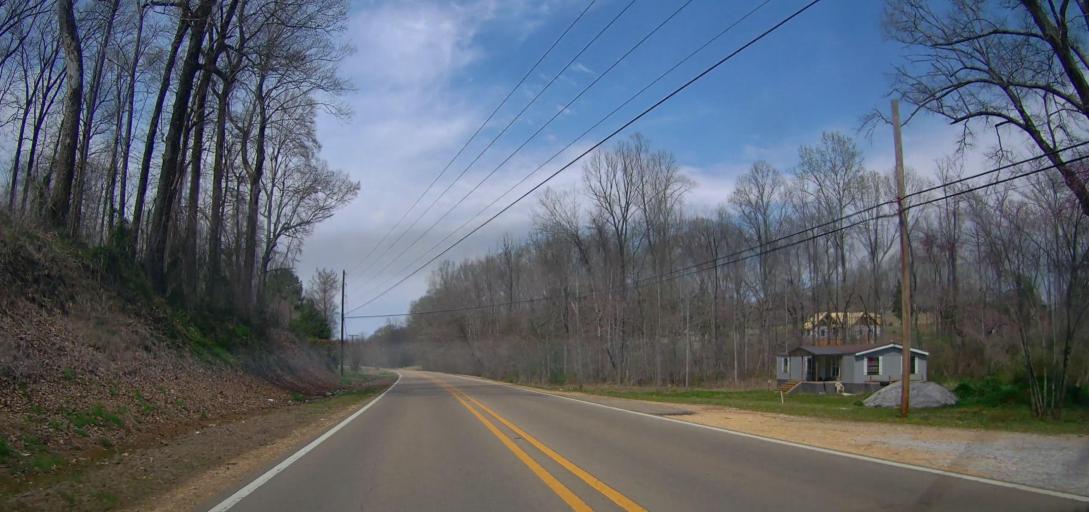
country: US
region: Mississippi
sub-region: Union County
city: New Albany
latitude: 34.4647
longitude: -88.9822
